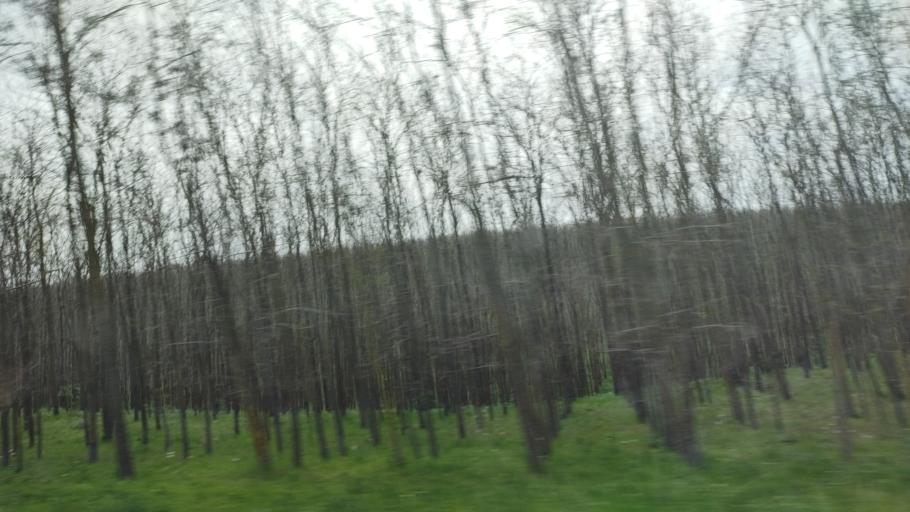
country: RO
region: Constanta
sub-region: Comuna Deleni
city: Pietreni
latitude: 44.0899
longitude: 28.0839
